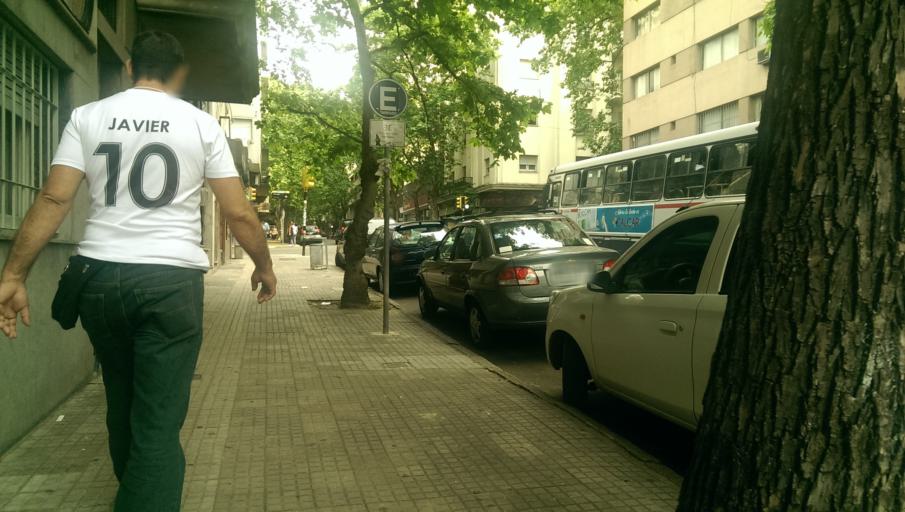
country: UY
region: Montevideo
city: Montevideo
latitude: -34.9035
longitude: -56.1883
